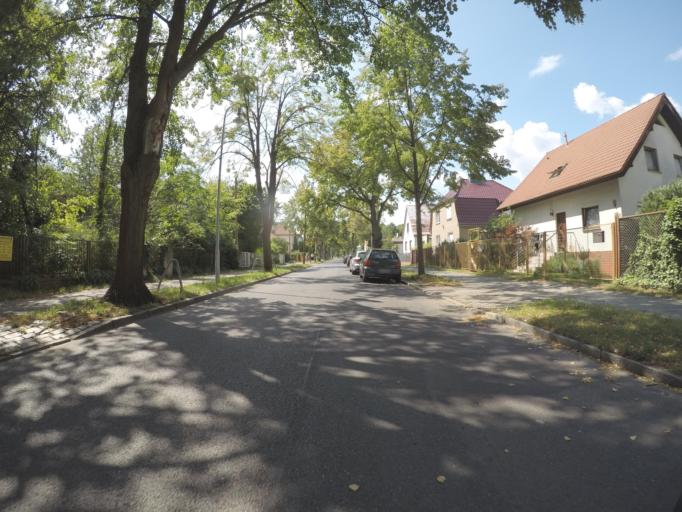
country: DE
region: Berlin
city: Kaulsdorf
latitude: 52.5112
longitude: 13.5952
